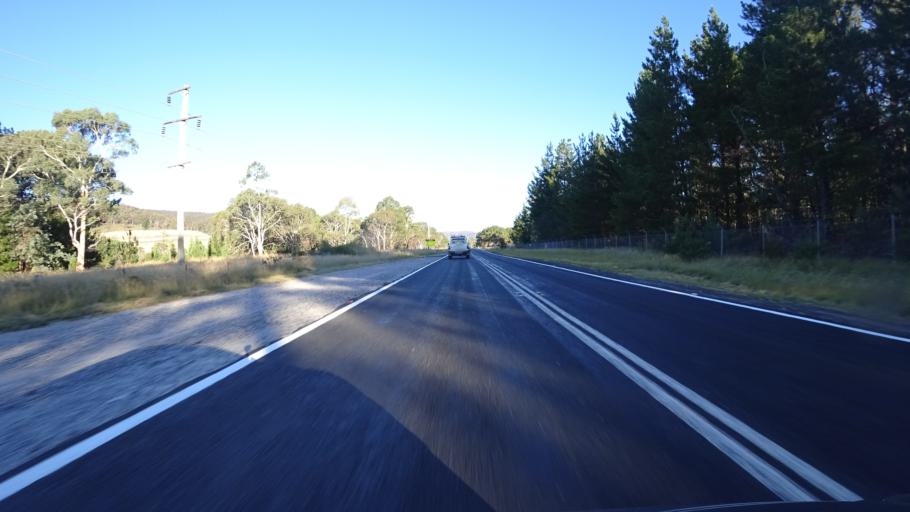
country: AU
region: New South Wales
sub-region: Lithgow
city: Portland
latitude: -33.3576
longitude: 150.0535
